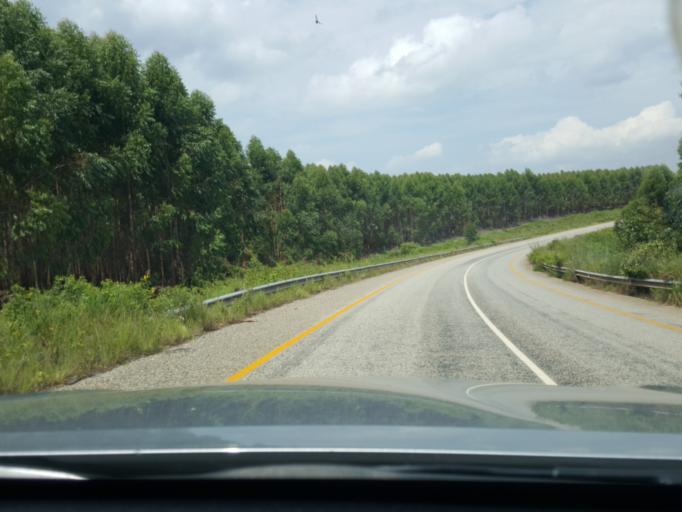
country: ZA
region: Mpumalanga
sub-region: Ehlanzeni District
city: White River
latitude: -25.1863
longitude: 30.8999
